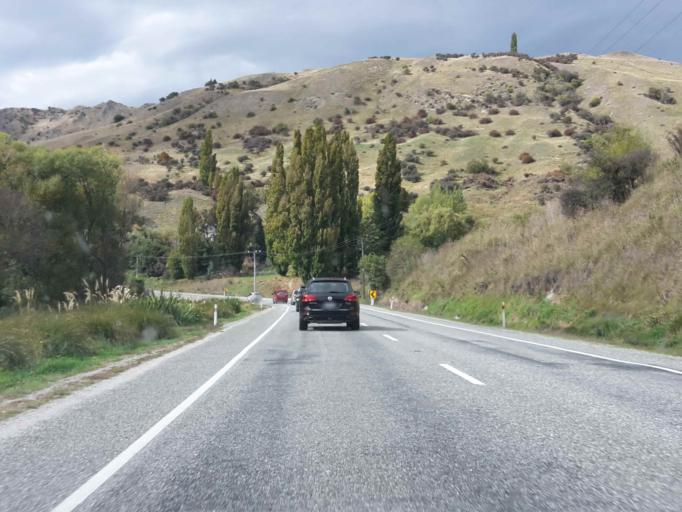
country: NZ
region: Otago
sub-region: Queenstown-Lakes District
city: Arrowtown
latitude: -44.9954
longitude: 168.8015
